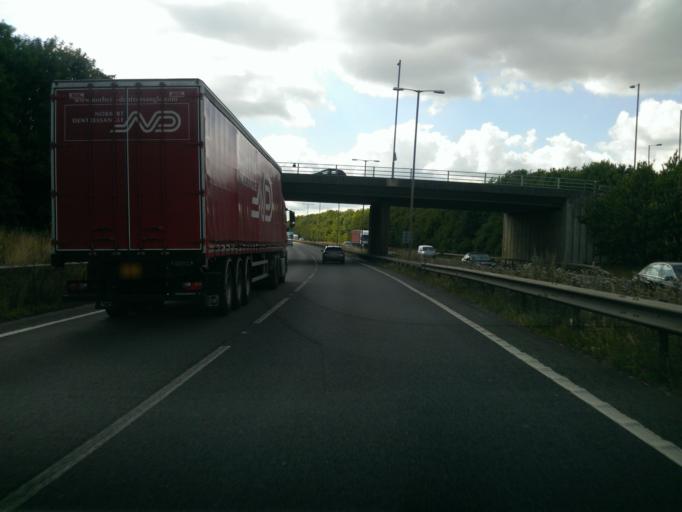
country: GB
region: England
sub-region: Northamptonshire
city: Rothwell
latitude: 52.4170
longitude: -0.8010
